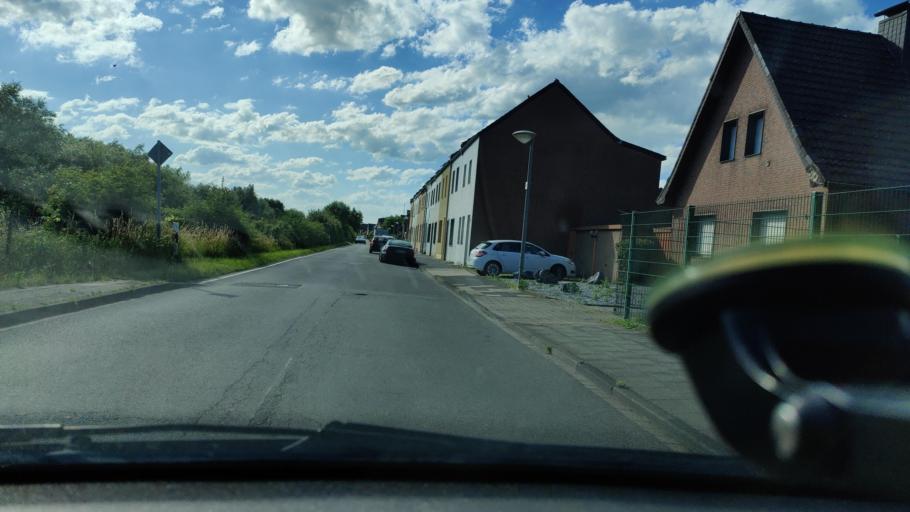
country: DE
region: North Rhine-Westphalia
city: Rheinberg
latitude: 51.5505
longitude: 6.5913
